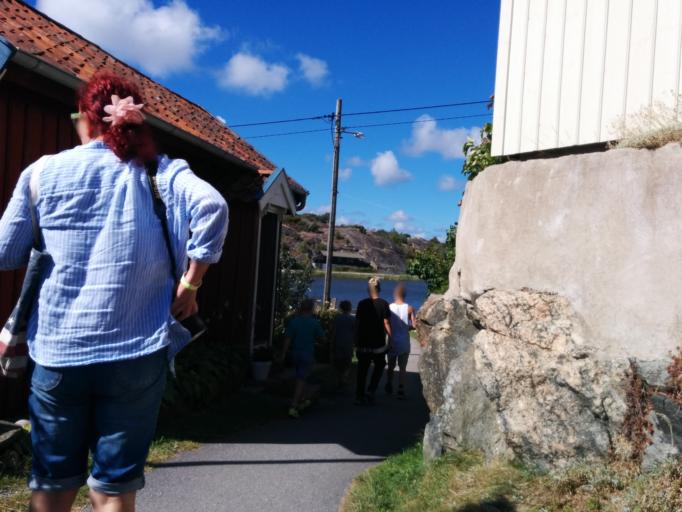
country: SE
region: Vaestra Goetaland
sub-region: Lysekils Kommun
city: Lysekil
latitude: 58.1244
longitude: 11.4417
